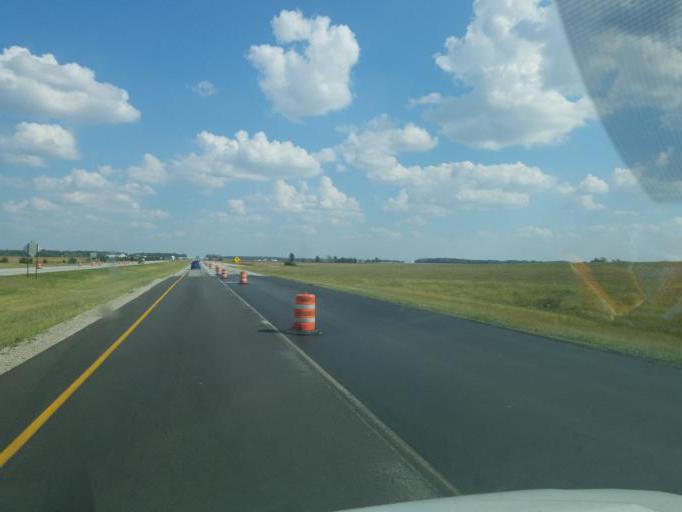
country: US
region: Ohio
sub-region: Allen County
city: Delphos
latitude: 40.8732
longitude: -84.4353
